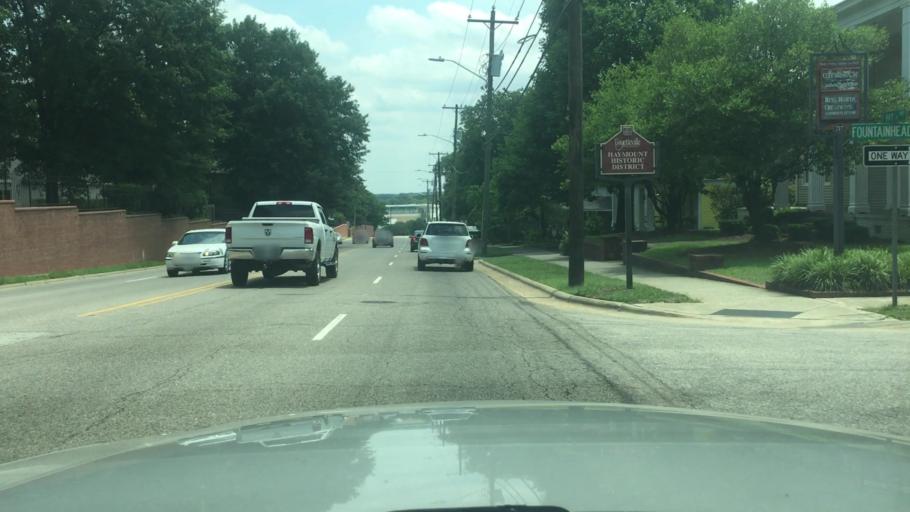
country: US
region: North Carolina
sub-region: Cumberland County
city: Fayetteville
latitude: 35.0559
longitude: -78.8908
